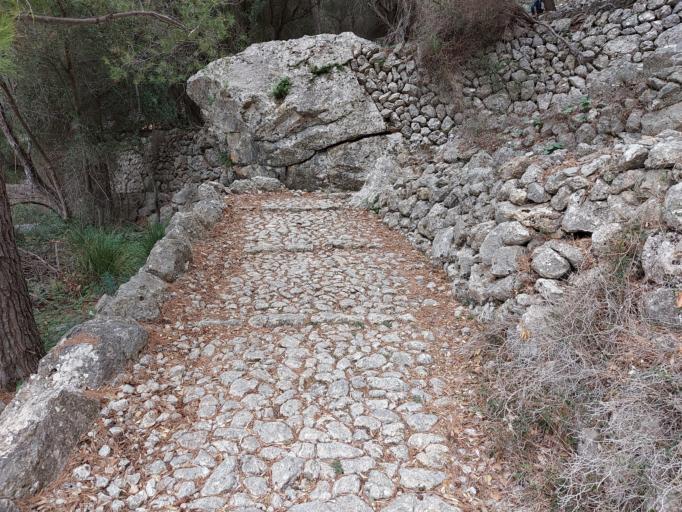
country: ES
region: Balearic Islands
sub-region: Illes Balears
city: Fornalutx
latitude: 39.7653
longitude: 2.7544
